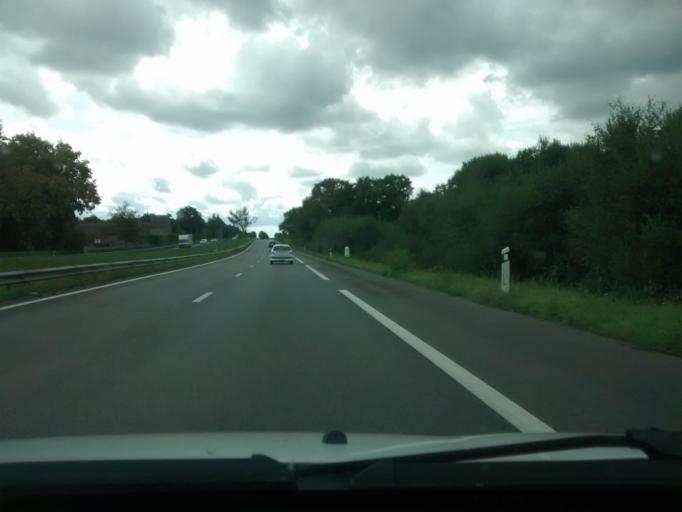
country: FR
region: Brittany
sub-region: Departement d'Ille-et-Vilaine
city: Miniac-Morvan
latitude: 48.4830
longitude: -1.9088
